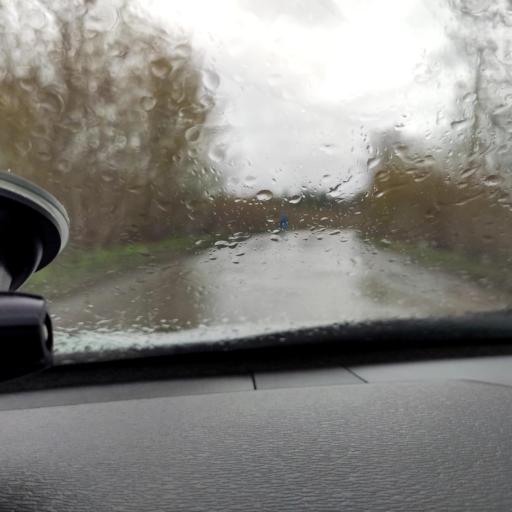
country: RU
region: Samara
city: Smyshlyayevka
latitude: 53.2645
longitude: 50.4881
